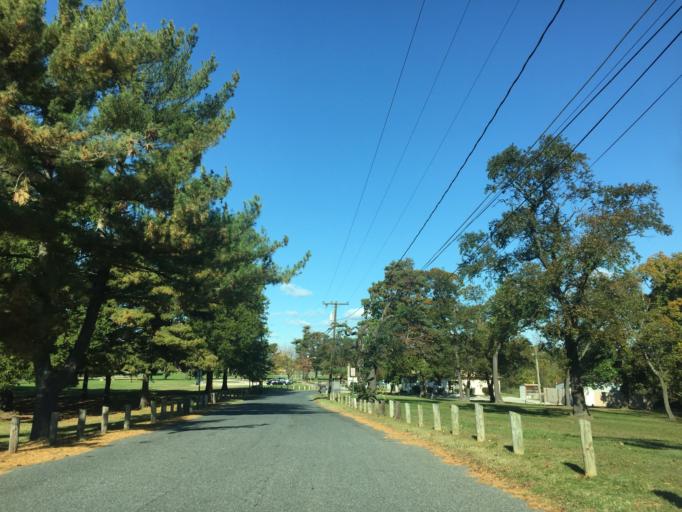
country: US
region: Maryland
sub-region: Baltimore County
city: Dundalk
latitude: 39.2546
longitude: -76.5058
